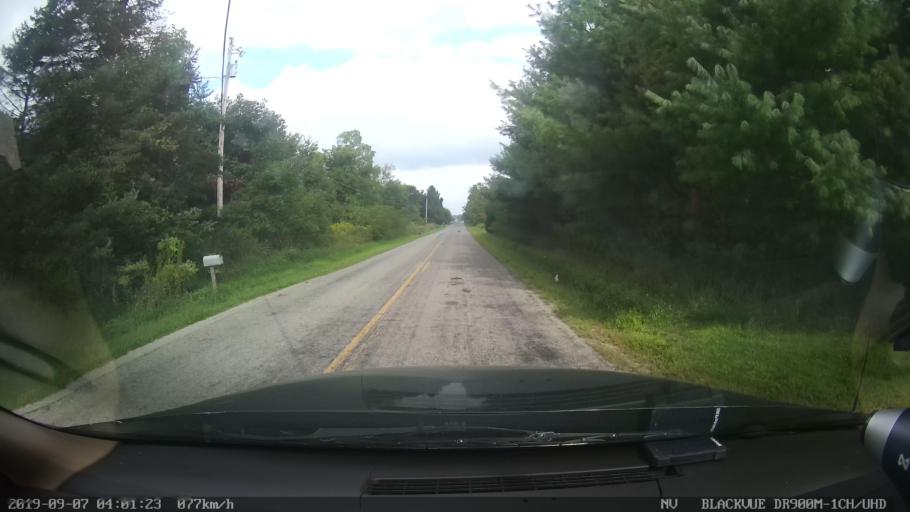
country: US
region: Ohio
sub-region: Licking County
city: Johnstown
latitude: 40.1790
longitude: -82.5860
